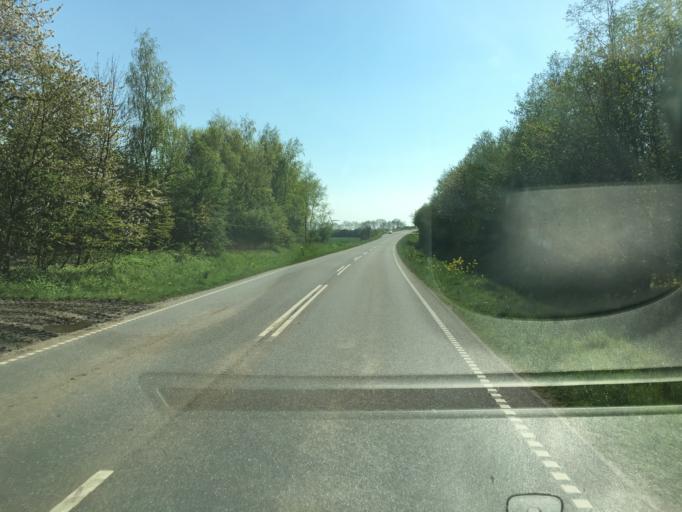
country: DK
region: South Denmark
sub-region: Haderslev Kommune
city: Vojens
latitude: 55.3145
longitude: 9.2927
